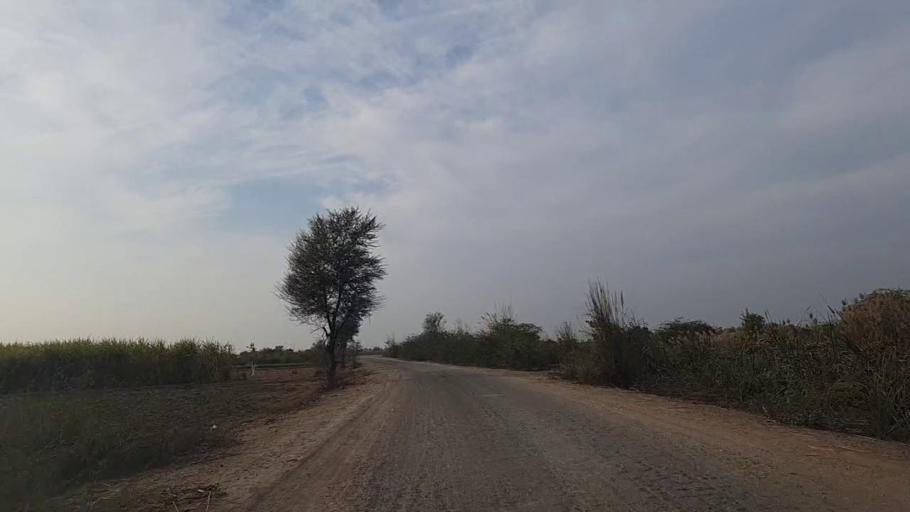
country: PK
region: Sindh
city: Daur
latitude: 26.5025
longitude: 68.4423
